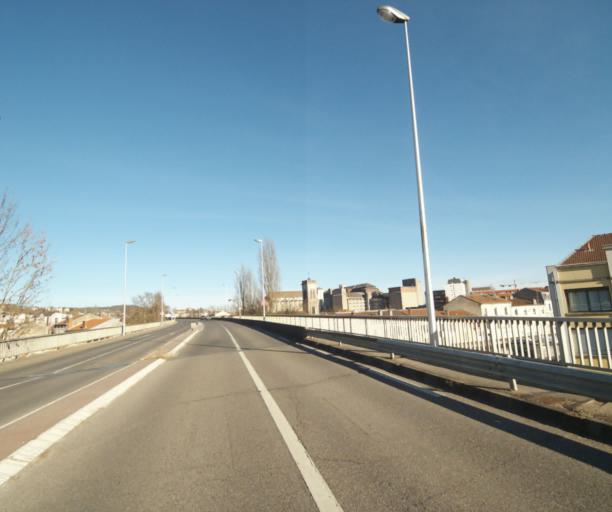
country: FR
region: Lorraine
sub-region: Departement de Meurthe-et-Moselle
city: Malzeville
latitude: 48.7011
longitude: 6.1875
